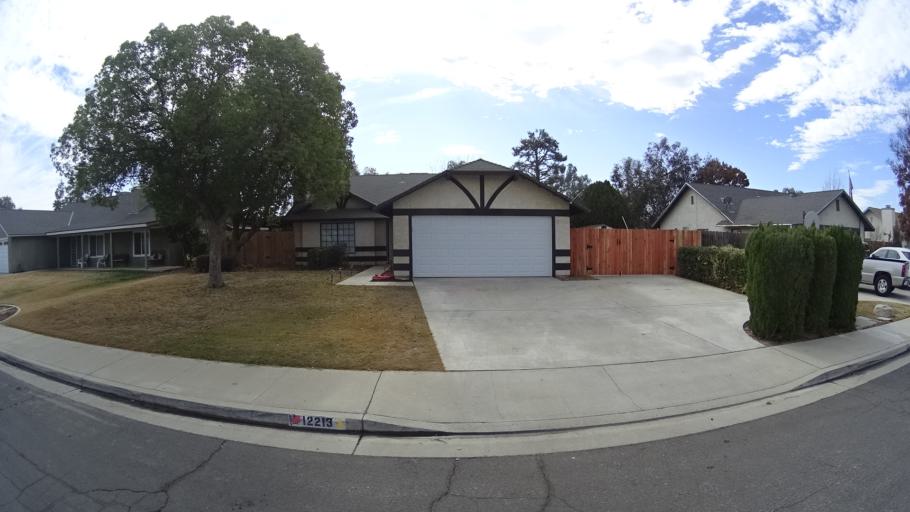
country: US
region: California
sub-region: Kern County
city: Rosedale
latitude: 35.3965
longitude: -119.1387
